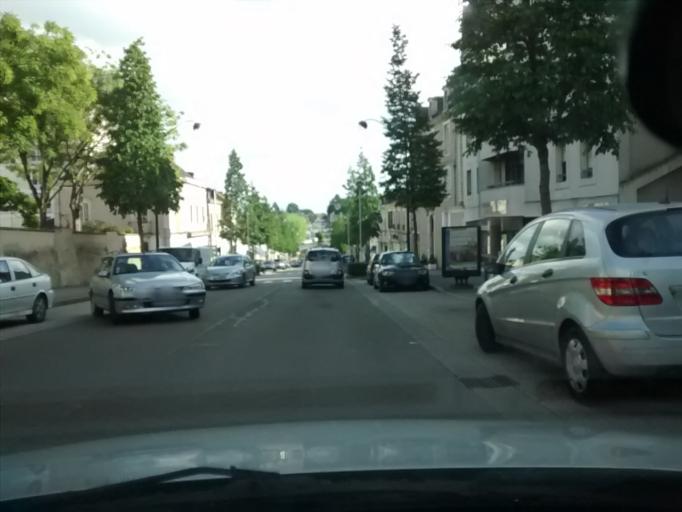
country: FR
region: Pays de la Loire
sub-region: Departement de la Mayenne
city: Chateau-Gontier
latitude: 47.8261
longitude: -0.7080
